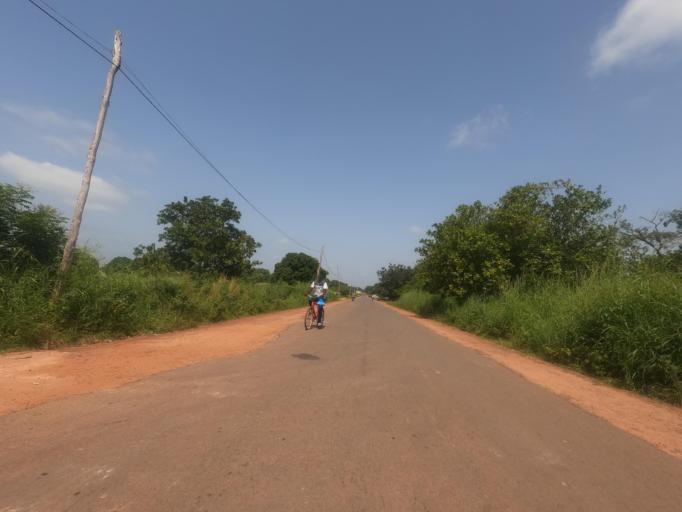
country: SN
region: Ziguinchor
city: Adeane
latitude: 12.3982
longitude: -15.7895
